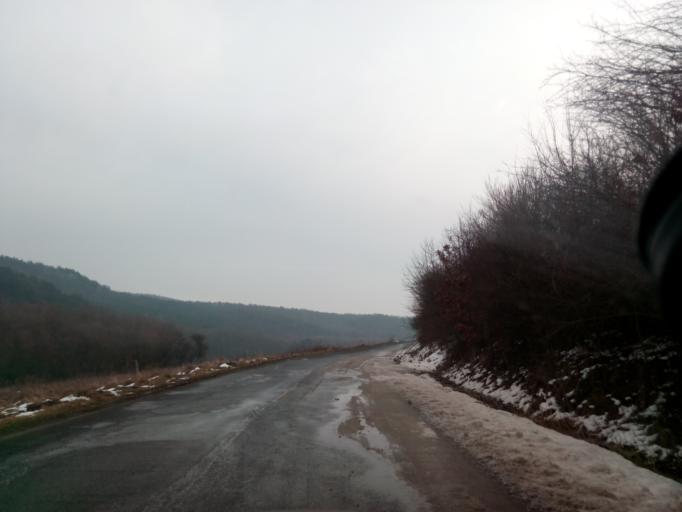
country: HU
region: Borsod-Abauj-Zemplen
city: Gonc
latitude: 48.5036
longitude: 21.3338
